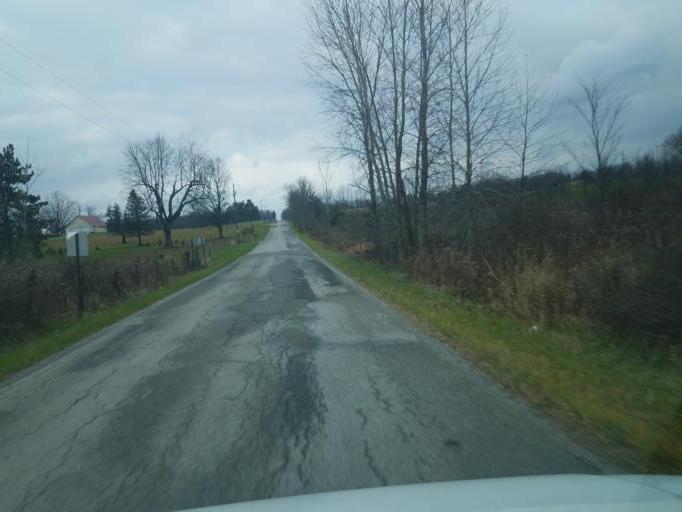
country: US
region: Ohio
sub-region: Morrow County
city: Mount Gilead
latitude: 40.5677
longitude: -82.8057
